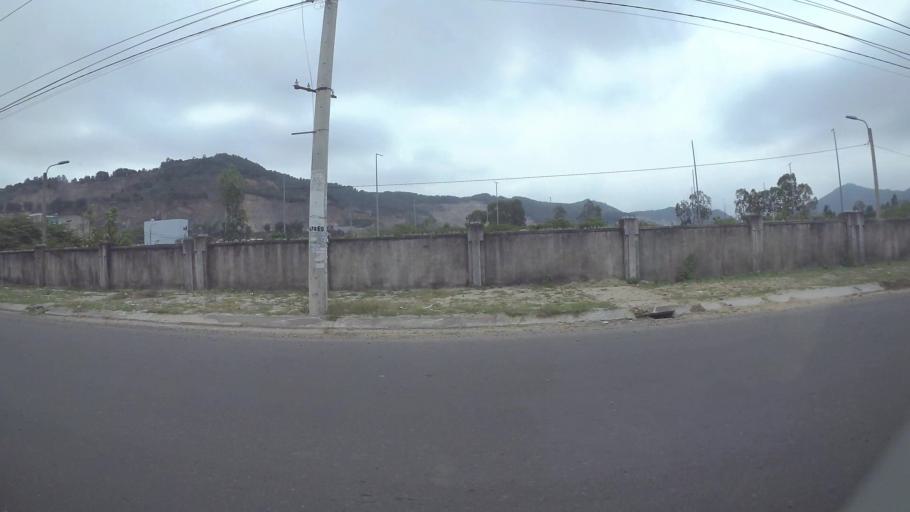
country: VN
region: Da Nang
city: Lien Chieu
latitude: 16.0463
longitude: 108.1647
